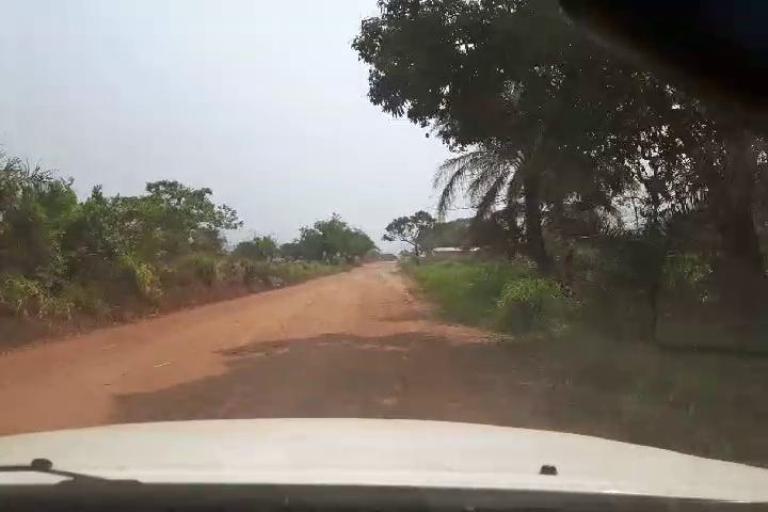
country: SL
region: Northern Province
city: Bumbuna
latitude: 9.0111
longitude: -11.7708
